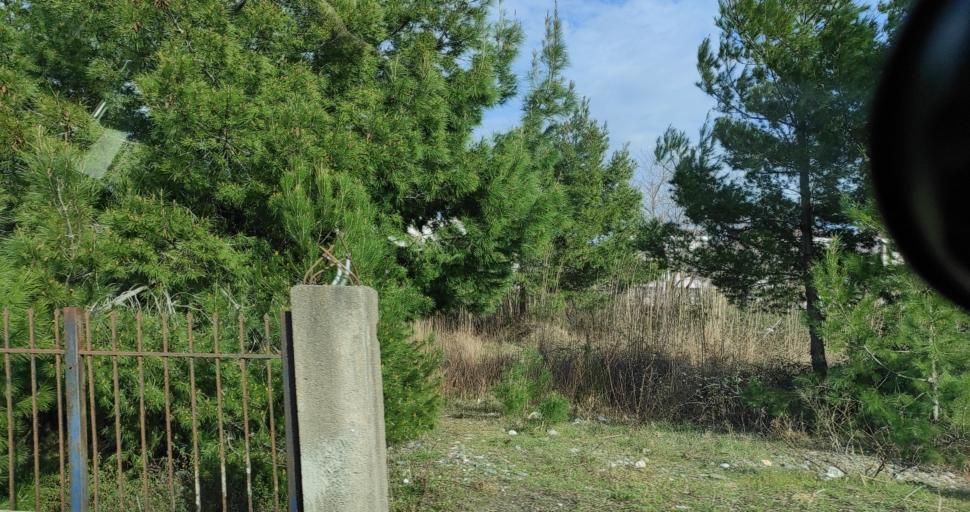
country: AL
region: Lezhe
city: Shengjin
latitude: 41.7906
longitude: 19.6031
